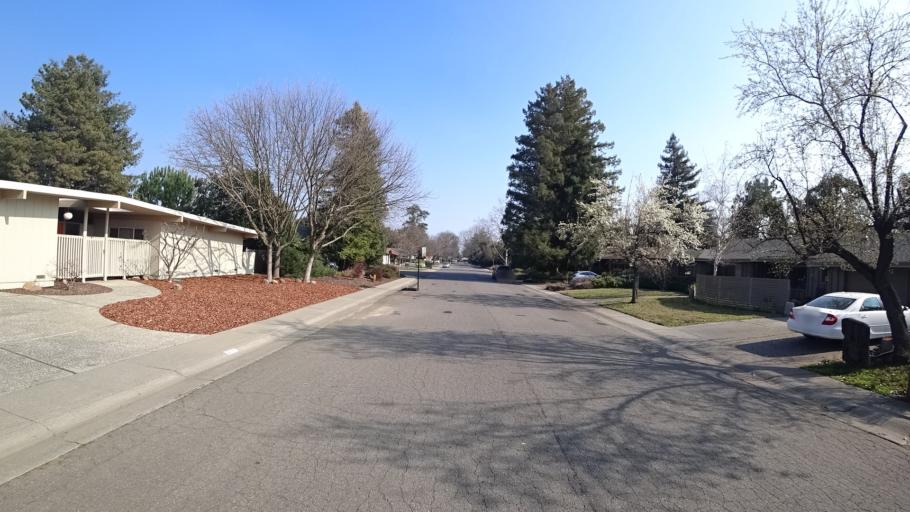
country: US
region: California
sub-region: Yolo County
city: Davis
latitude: 38.5531
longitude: -121.7544
